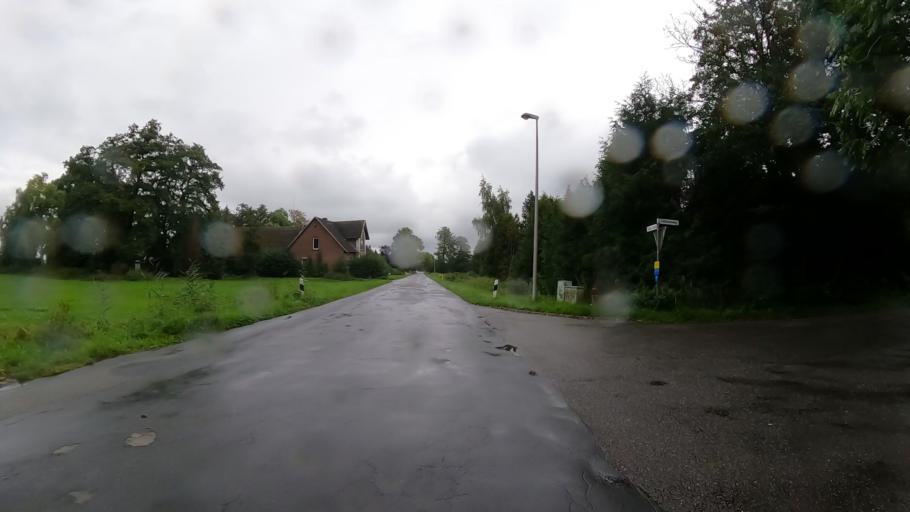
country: DE
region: Lower Saxony
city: Buxtehude
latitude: 53.4764
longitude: 9.7210
